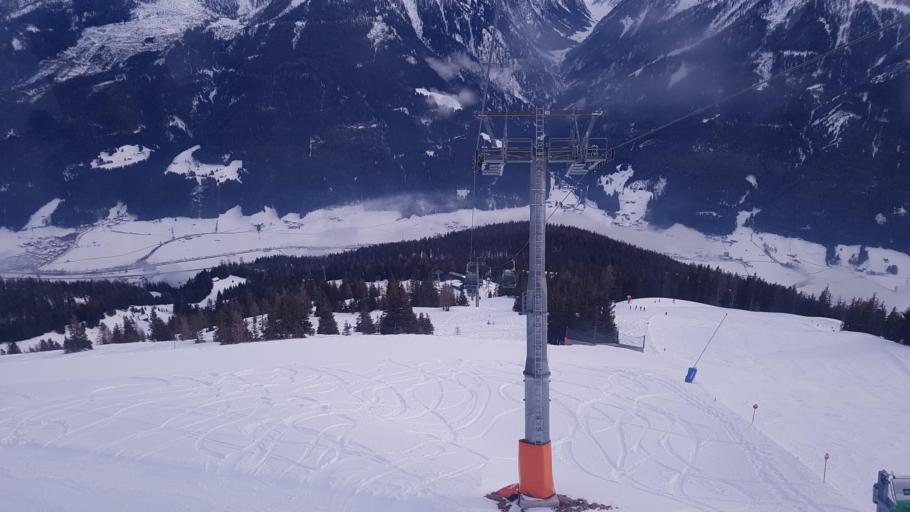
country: AT
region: Salzburg
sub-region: Politischer Bezirk Zell am See
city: Neukirchen am Grossvenediger
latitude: 47.2768
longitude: 12.2991
